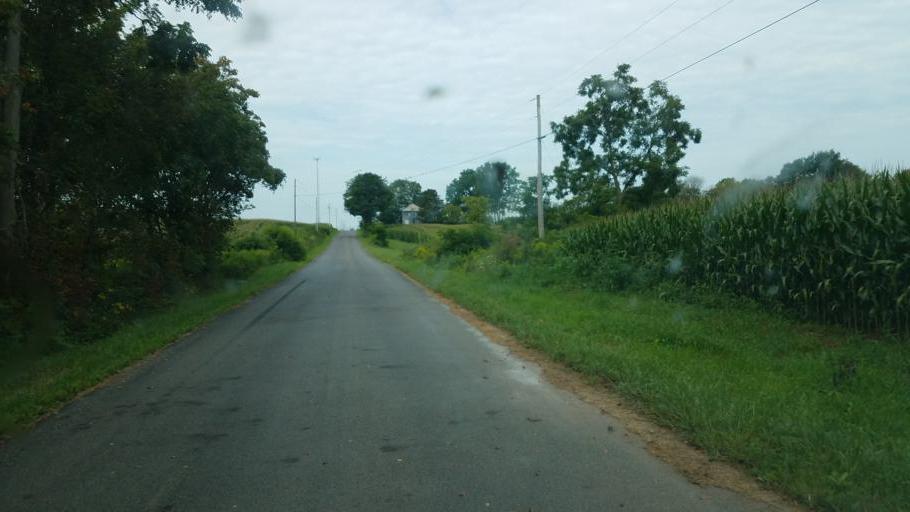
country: US
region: Ohio
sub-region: Morrow County
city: Mount Gilead
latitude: 40.4765
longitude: -82.7237
